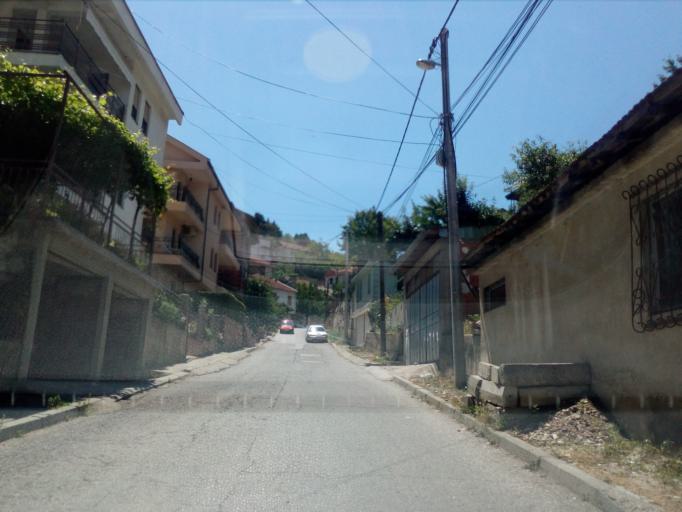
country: MK
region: Veles
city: Veles
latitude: 41.7142
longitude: 21.7745
